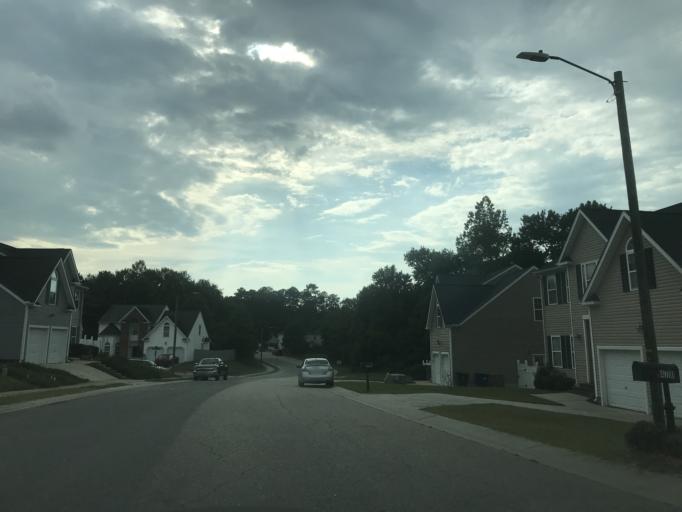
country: US
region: North Carolina
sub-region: Wake County
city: Knightdale
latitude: 35.8426
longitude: -78.5603
